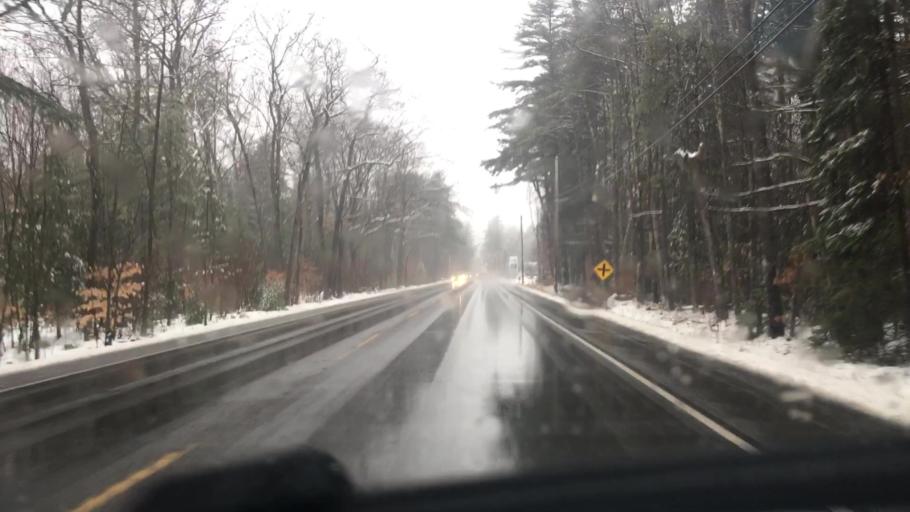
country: US
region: Maine
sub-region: York County
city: Buxton
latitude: 43.7168
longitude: -70.5218
